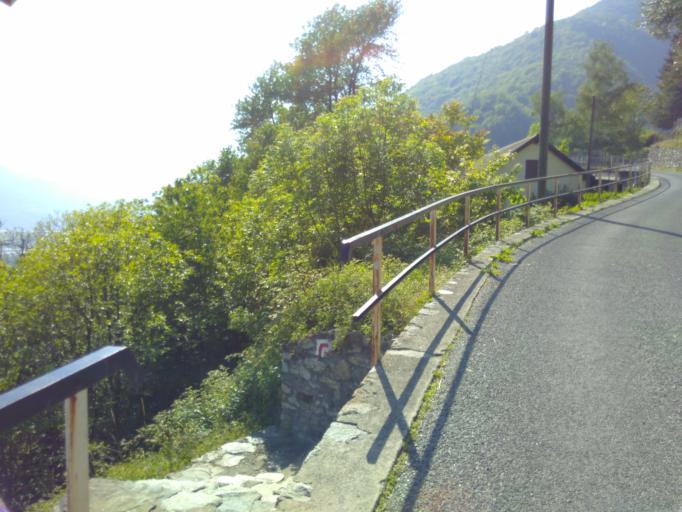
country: CH
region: Ticino
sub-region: Bellinzona District
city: Sementina
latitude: 46.1894
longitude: 8.9927
